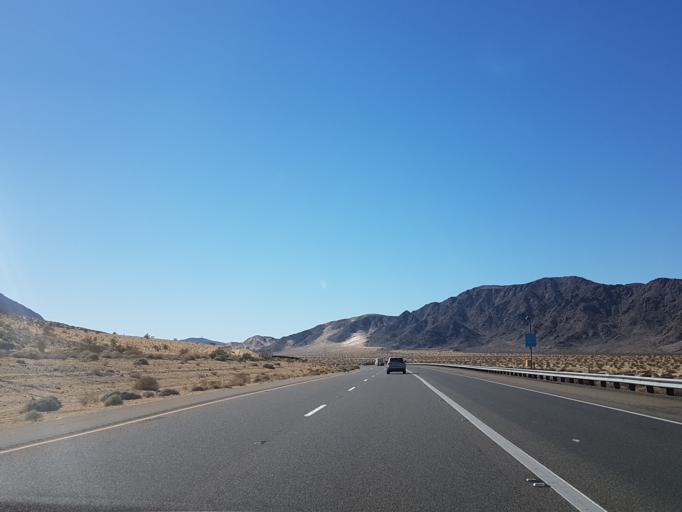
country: US
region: California
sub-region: San Bernardino County
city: Fort Irwin
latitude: 35.0989
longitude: -116.2888
